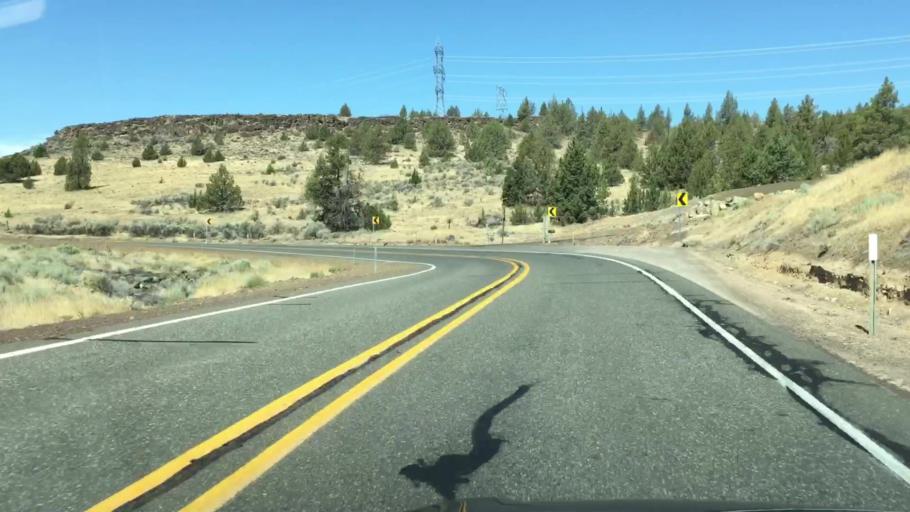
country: US
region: Oregon
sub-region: Wasco County
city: The Dalles
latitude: 45.1694
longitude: -121.0995
